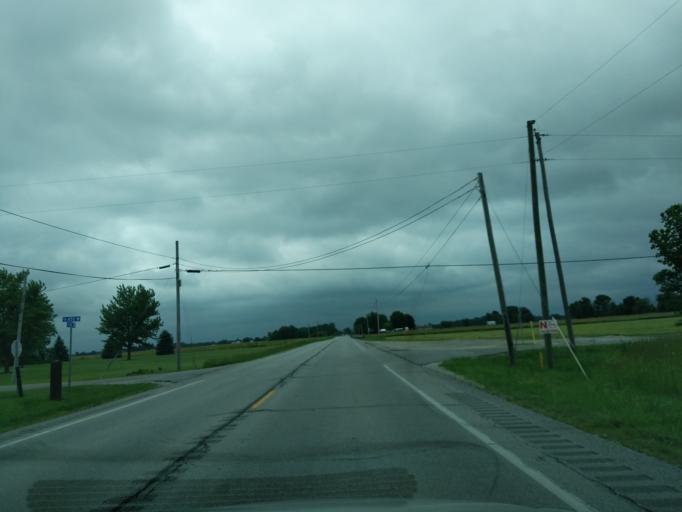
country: US
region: Indiana
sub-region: Madison County
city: Frankton
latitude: 40.2775
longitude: -85.7571
